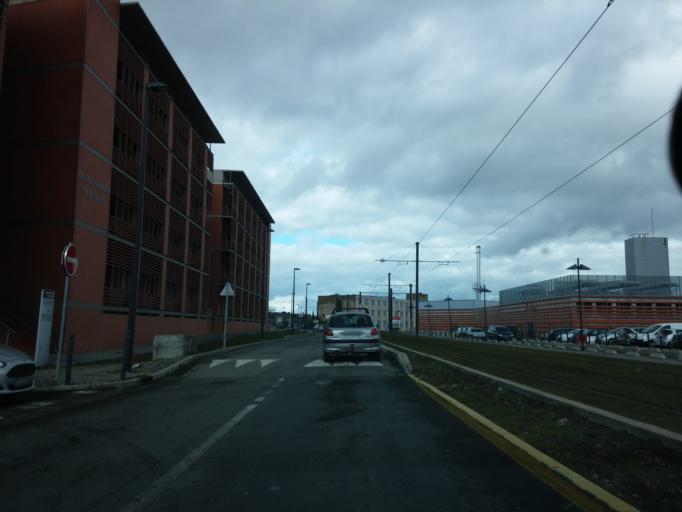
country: FR
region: Midi-Pyrenees
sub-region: Departement de la Haute-Garonne
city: Blagnac
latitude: 43.6103
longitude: 1.4018
